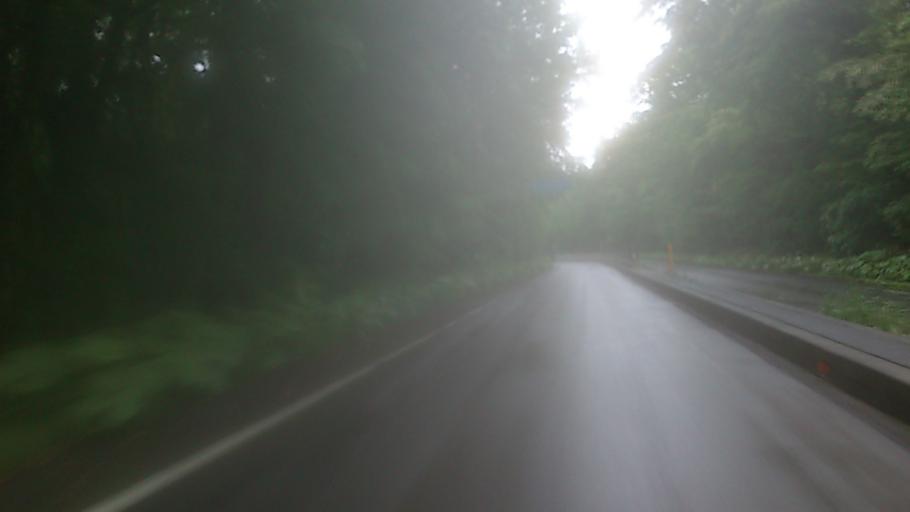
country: JP
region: Hokkaido
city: Tomakomai
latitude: 42.7643
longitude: 141.4360
